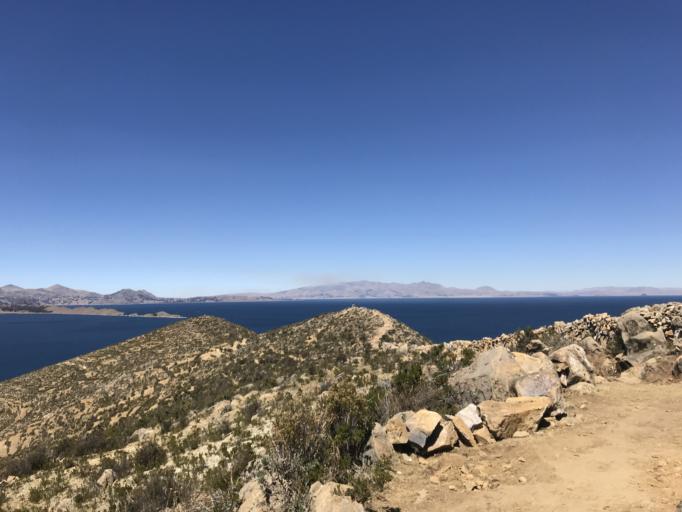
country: BO
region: La Paz
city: Yumani
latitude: -16.0463
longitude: -69.1465
